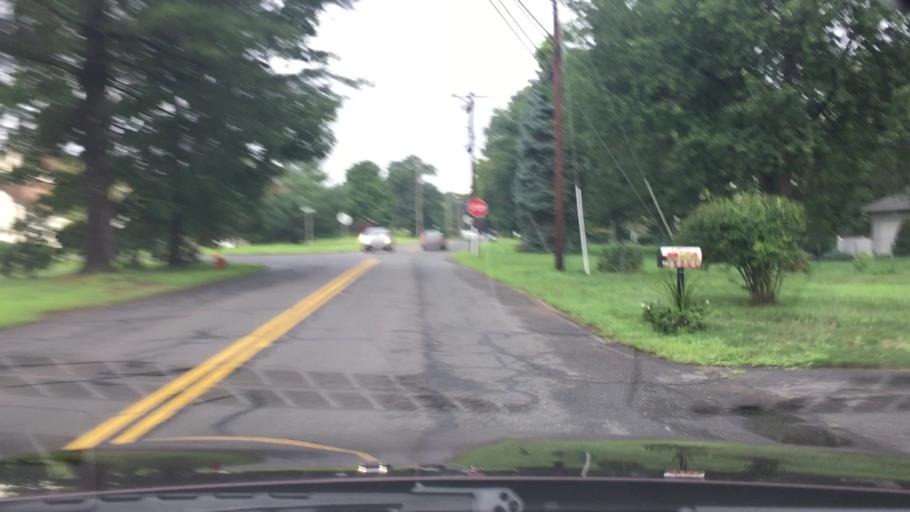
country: US
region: Connecticut
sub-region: Hartford County
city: South Windsor
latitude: 41.8266
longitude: -72.5881
